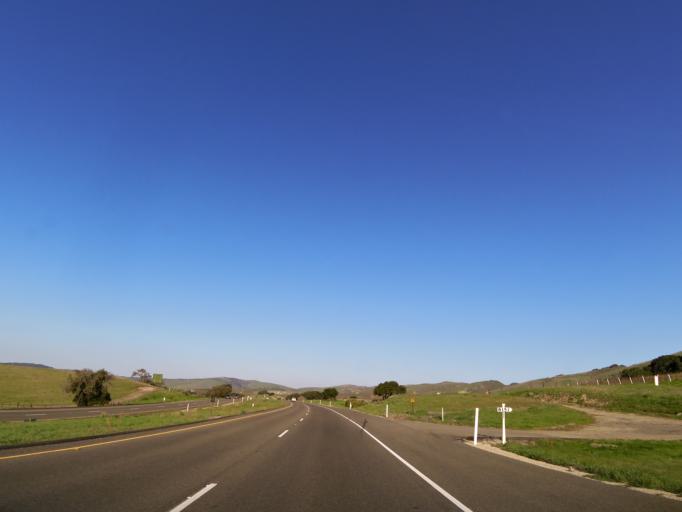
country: US
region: California
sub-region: Santa Barbara County
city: Los Alamos
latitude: 34.7811
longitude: -120.3156
